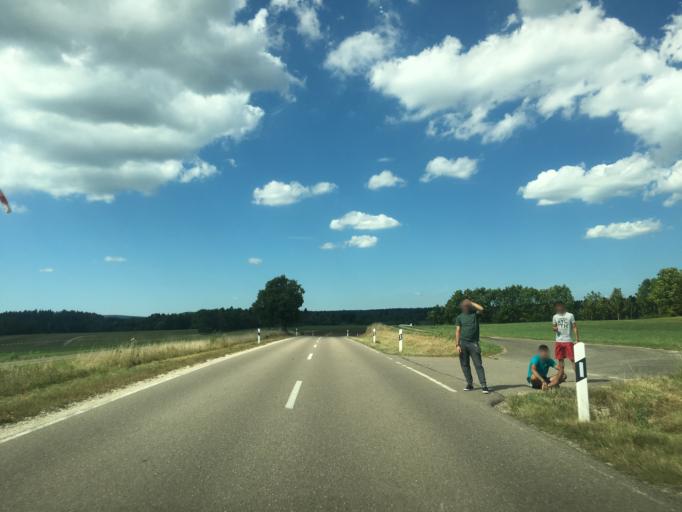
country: DE
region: Baden-Wuerttemberg
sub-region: Tuebingen Region
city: Hayingen
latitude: 48.2847
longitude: 9.4684
